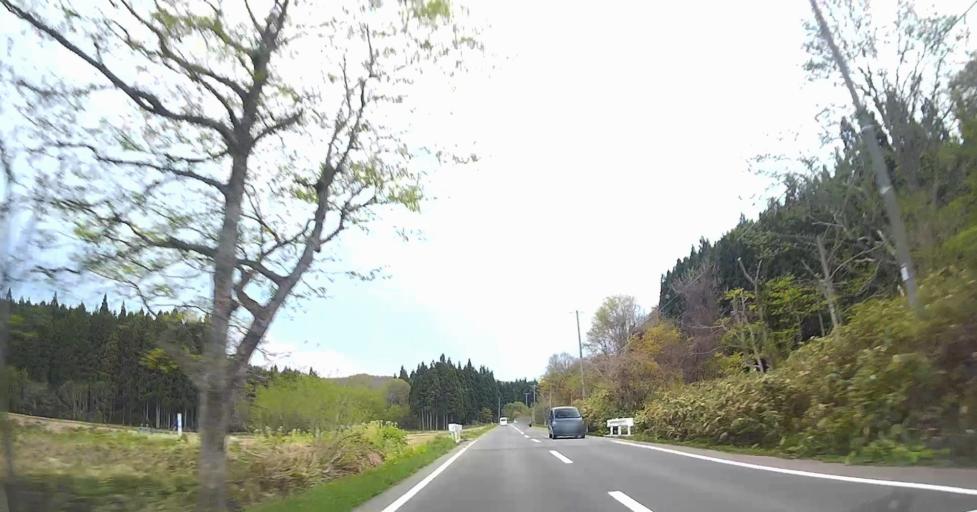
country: JP
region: Aomori
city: Goshogawara
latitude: 41.1225
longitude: 140.5218
